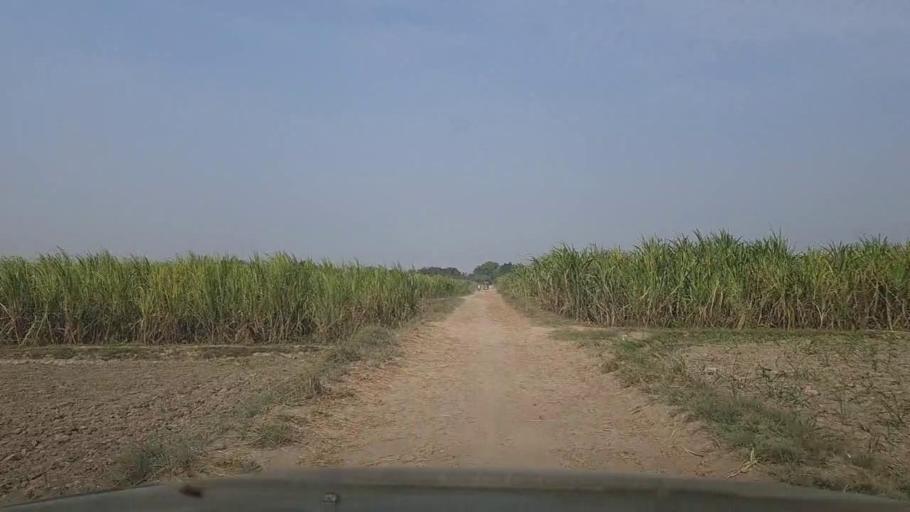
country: PK
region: Sindh
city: Bulri
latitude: 25.0212
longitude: 68.2819
